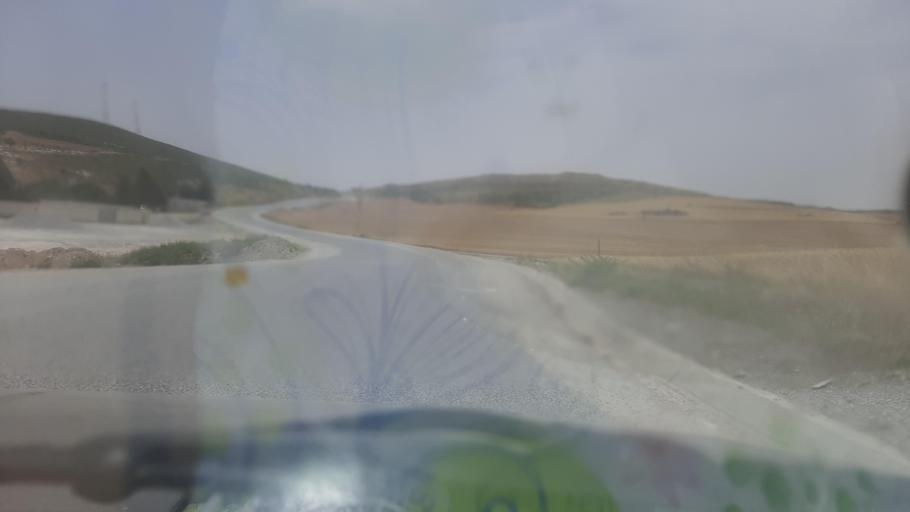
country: TN
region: Zaghwan
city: Zaghouan
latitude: 36.5378
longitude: 10.1534
